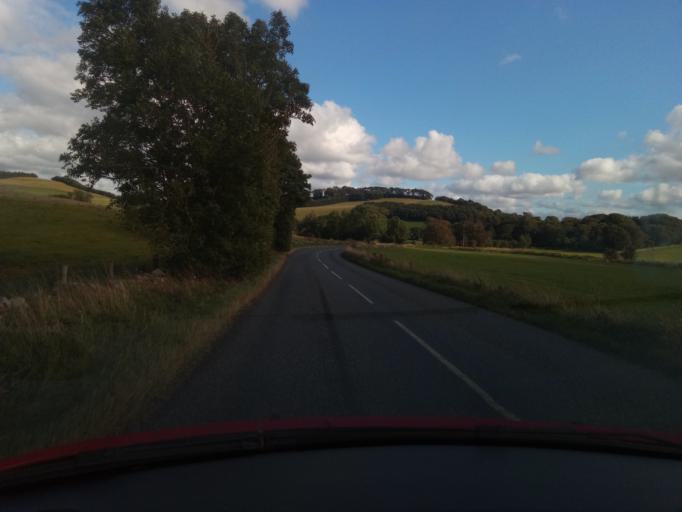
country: GB
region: Scotland
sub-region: The Scottish Borders
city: Kelso
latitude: 55.5622
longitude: -2.3348
